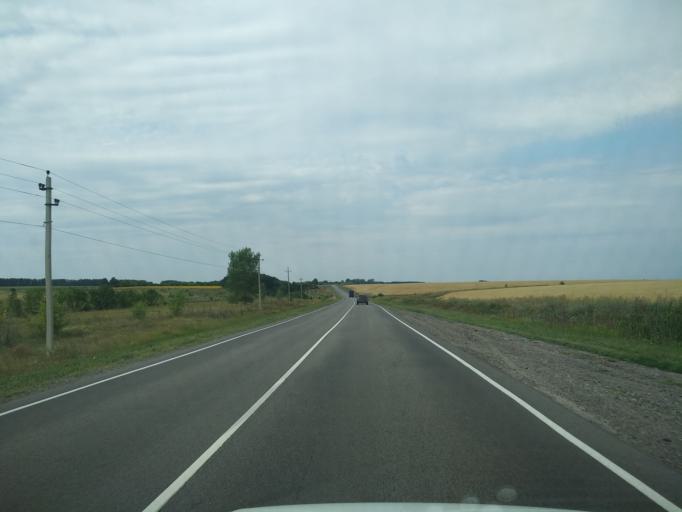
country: RU
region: Voronezj
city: Pereleshinskiy
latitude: 51.8211
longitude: 40.2694
